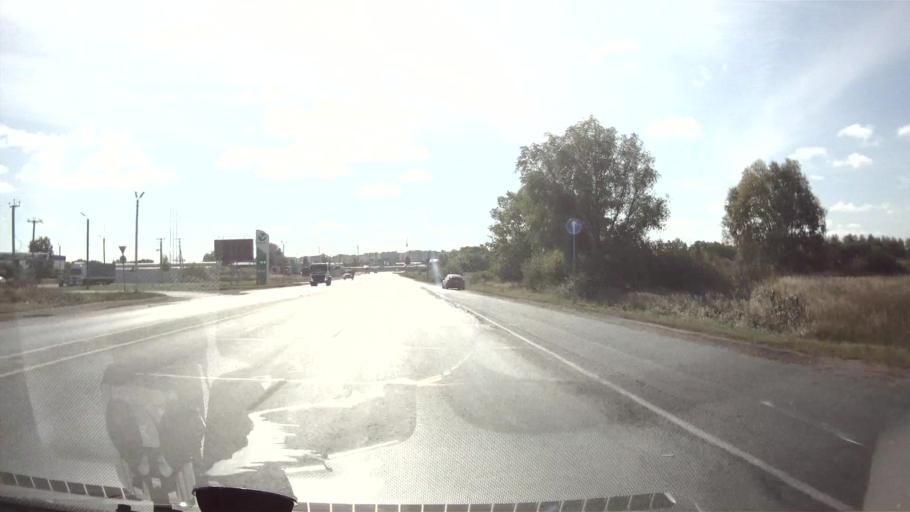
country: RU
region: Ulyanovsk
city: Isheyevka
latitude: 54.2953
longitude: 48.2501
